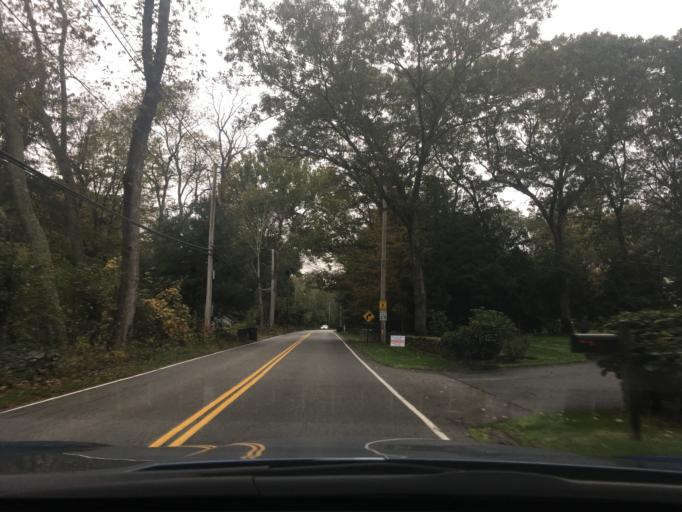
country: US
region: Rhode Island
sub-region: Kent County
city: East Greenwich
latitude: 41.6425
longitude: -71.4477
